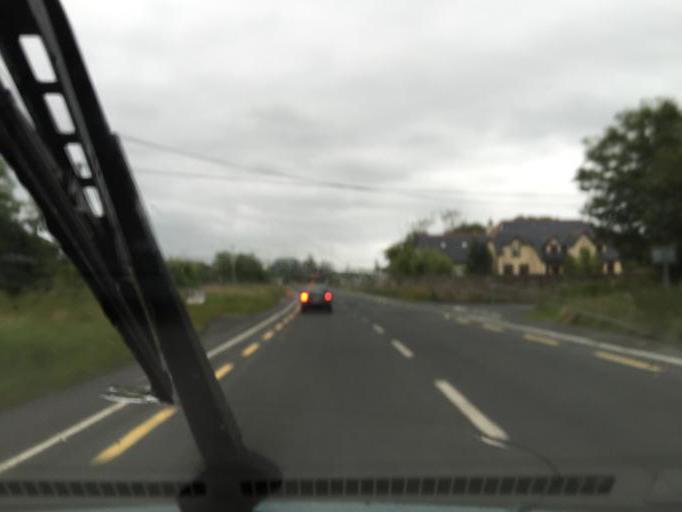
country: IE
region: Connaught
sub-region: Sligo
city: Strandhill
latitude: 54.2726
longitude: -8.5485
